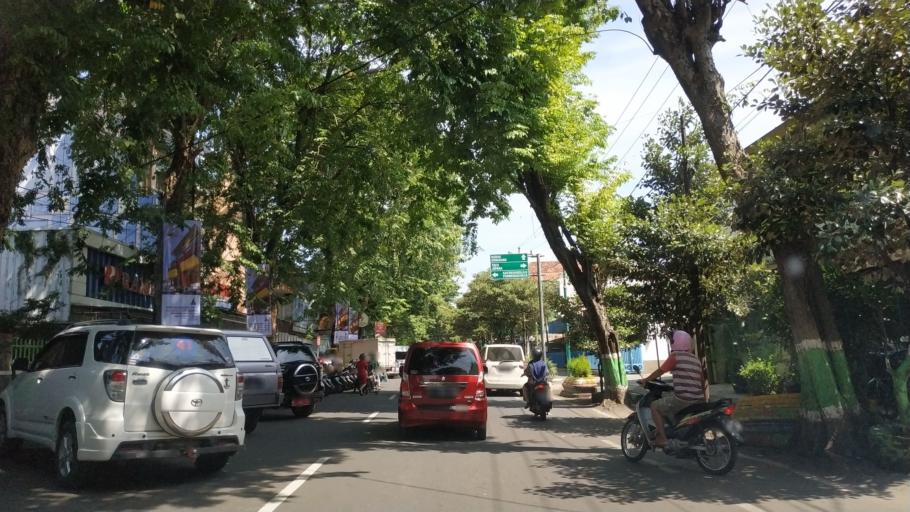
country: ID
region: Central Java
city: Pati
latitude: -6.7527
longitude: 111.0378
